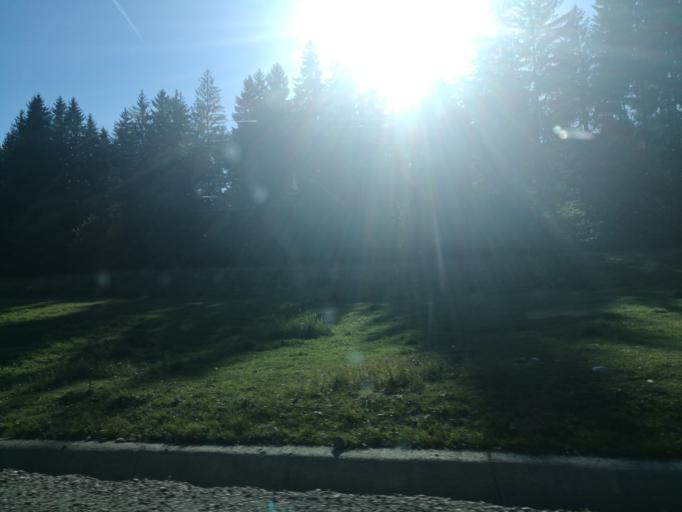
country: RO
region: Brasov
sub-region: Comuna Dumbravita
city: Dumbravita
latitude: 45.7599
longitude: 25.3851
